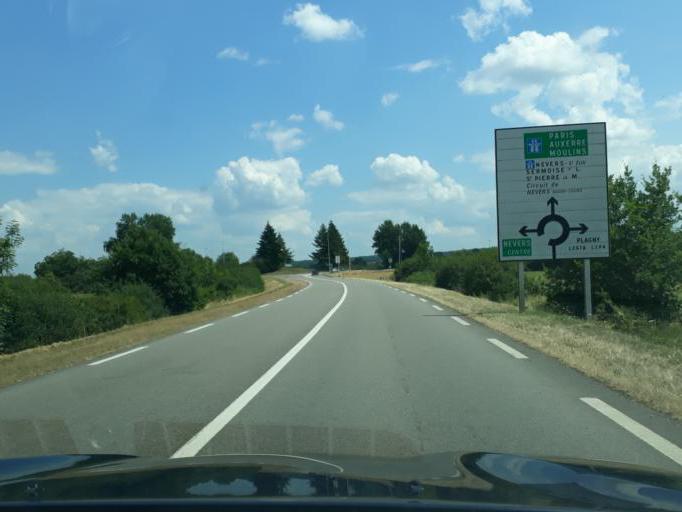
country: FR
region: Bourgogne
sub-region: Departement de la Nievre
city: Challuy
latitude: 46.9567
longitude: 3.1542
